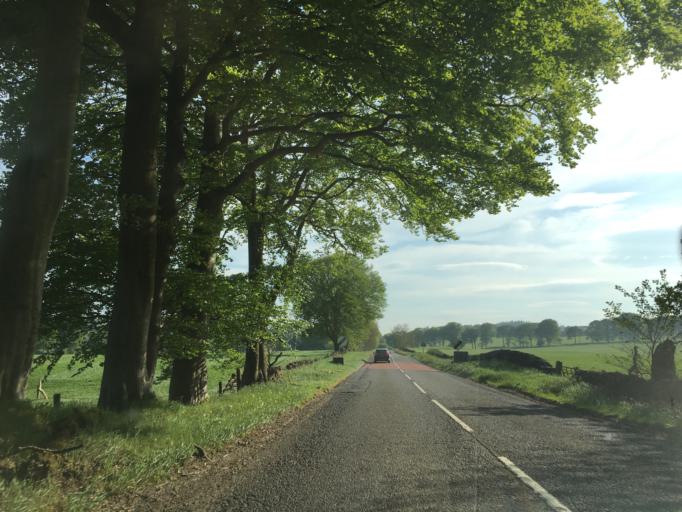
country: GB
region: Scotland
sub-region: The Scottish Borders
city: West Linton
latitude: 55.7157
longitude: -3.3438
